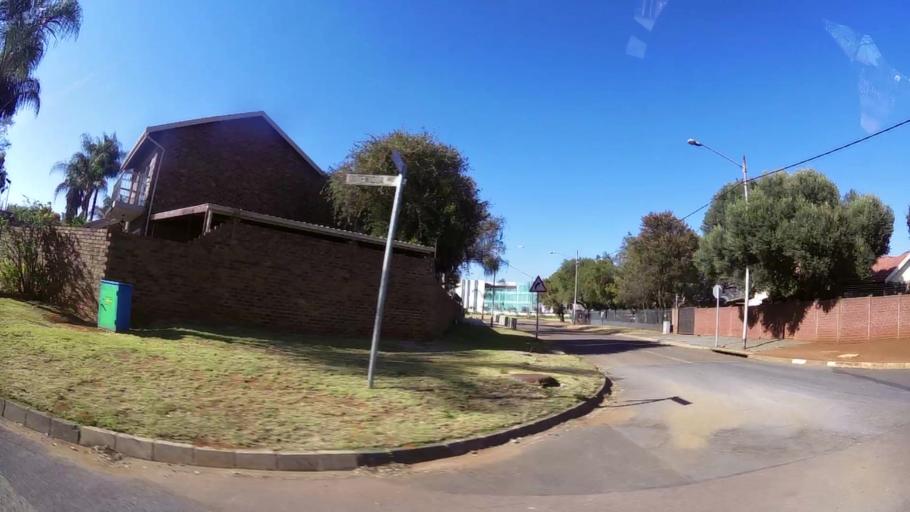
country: ZA
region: Gauteng
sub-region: City of Tshwane Metropolitan Municipality
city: Centurion
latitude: -25.8584
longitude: 28.2139
